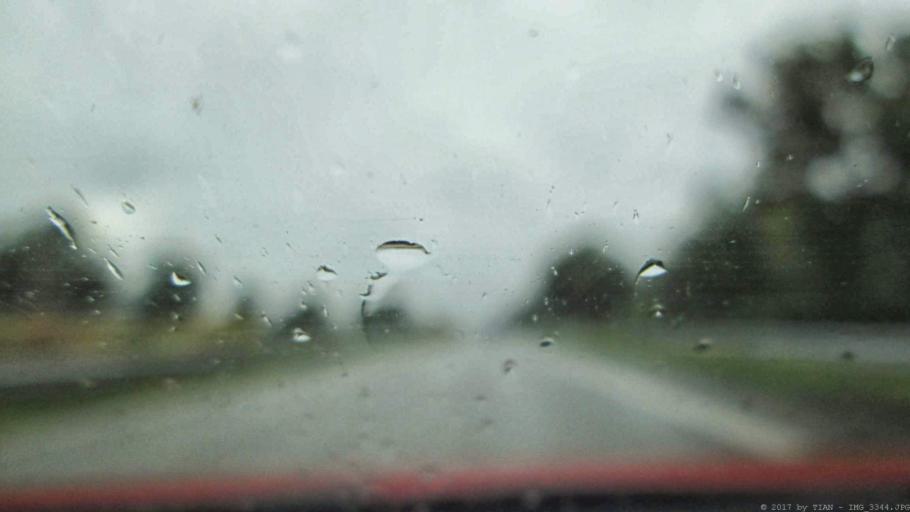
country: DE
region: Schleswig-Holstein
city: Bokelrehm
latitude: 54.0522
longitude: 9.3867
